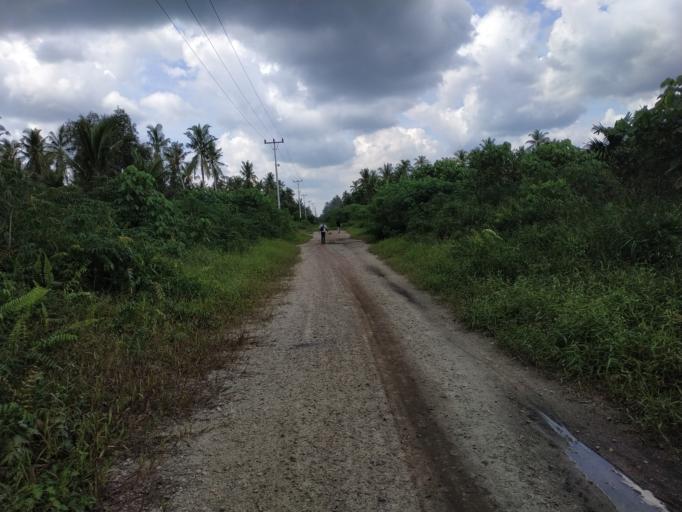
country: ID
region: Riau
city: Tembilahan
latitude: -0.2053
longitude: 103.2000
